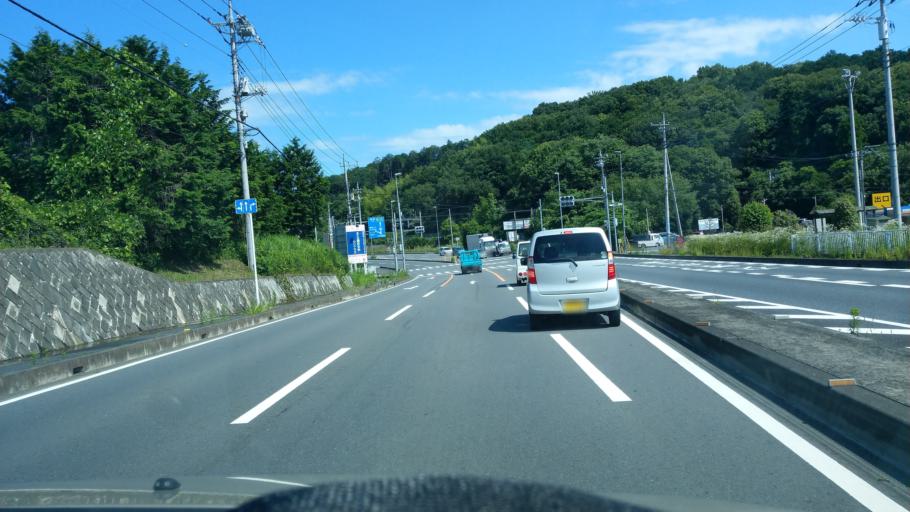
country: JP
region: Saitama
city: Ogawa
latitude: 36.0500
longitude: 139.3067
